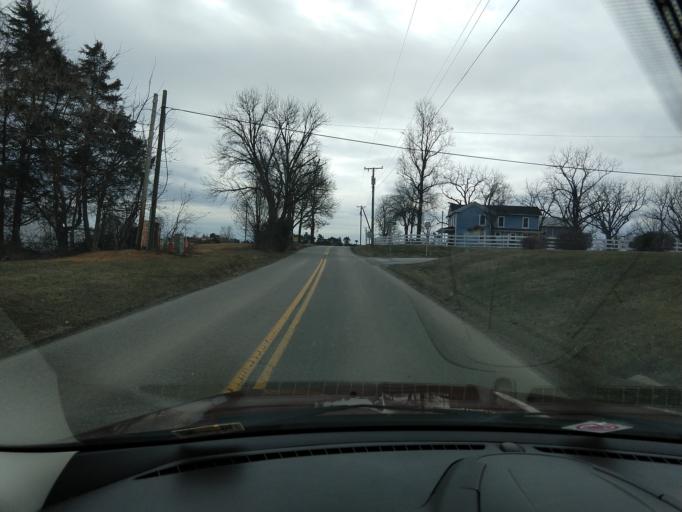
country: US
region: Virginia
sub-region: Augusta County
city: Crimora
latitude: 38.1896
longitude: -78.9116
